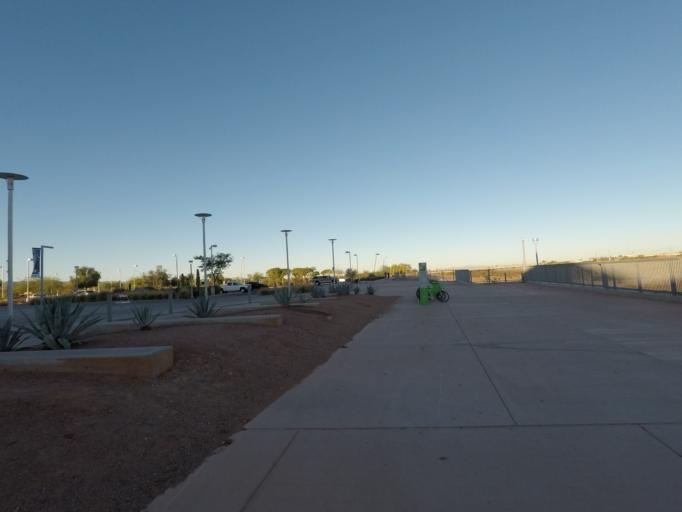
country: US
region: Arizona
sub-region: Maricopa County
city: Tempe Junction
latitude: 33.4324
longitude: -111.9494
